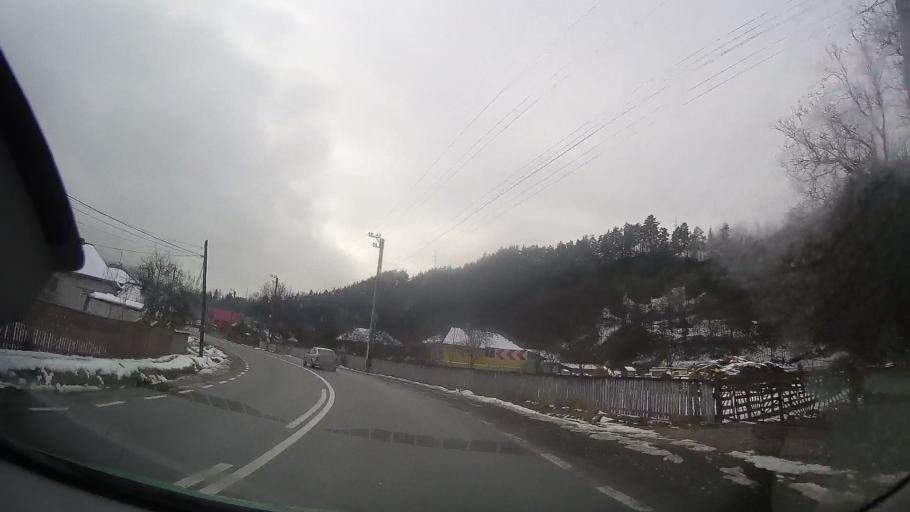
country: RO
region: Neamt
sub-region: Comuna Bicazu Ardelean
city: Bicazu Ardelean
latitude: 46.8629
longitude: 25.9378
